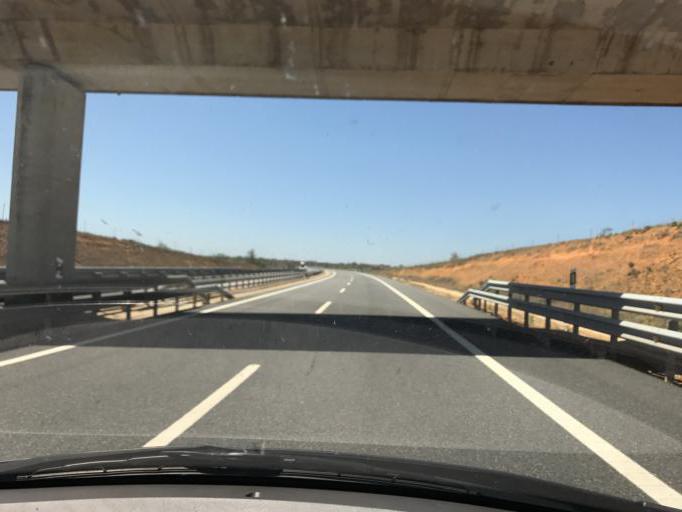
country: ES
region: Castille and Leon
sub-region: Provincia de Leon
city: Valverde de la Virgen
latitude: 42.5559
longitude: -5.6902
